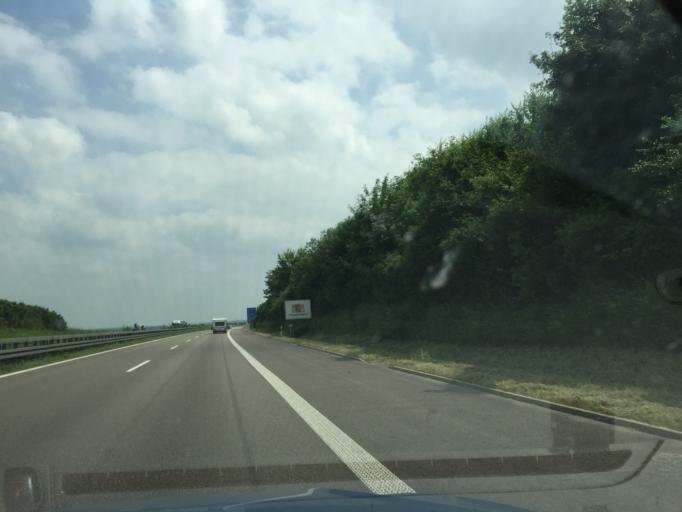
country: DE
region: Baden-Wuerttemberg
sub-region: Tuebingen Region
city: Langenau
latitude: 48.4775
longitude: 10.1070
